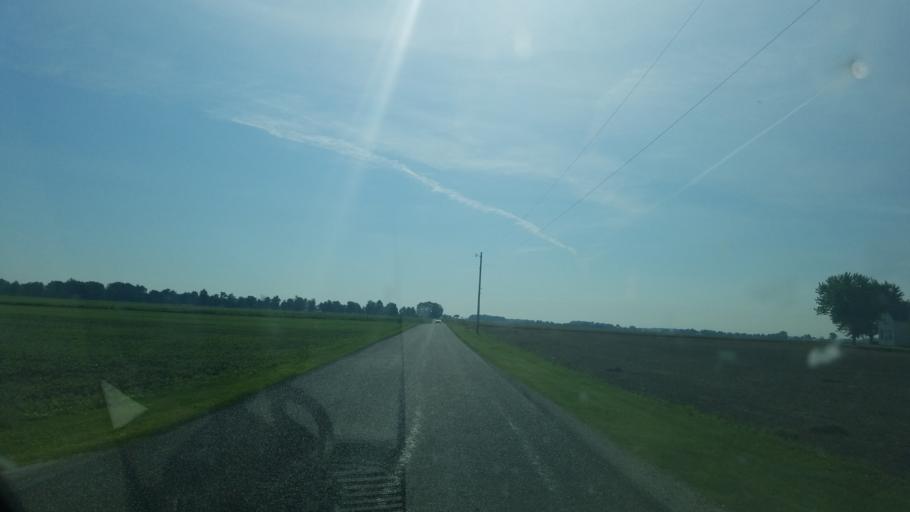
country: US
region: Ohio
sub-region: Hancock County
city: Findlay
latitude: 41.0214
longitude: -83.5450
